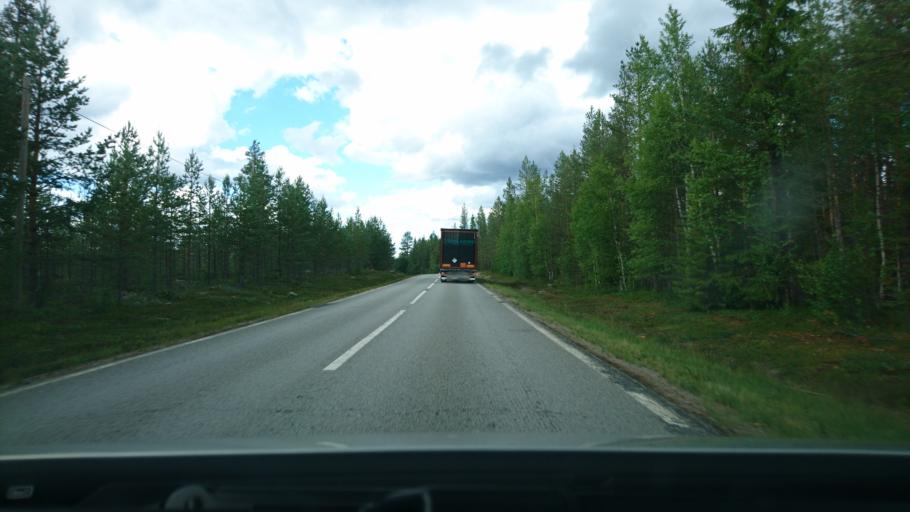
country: SE
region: Vaesterbotten
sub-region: Asele Kommun
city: Asele
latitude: 63.8537
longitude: 17.1625
